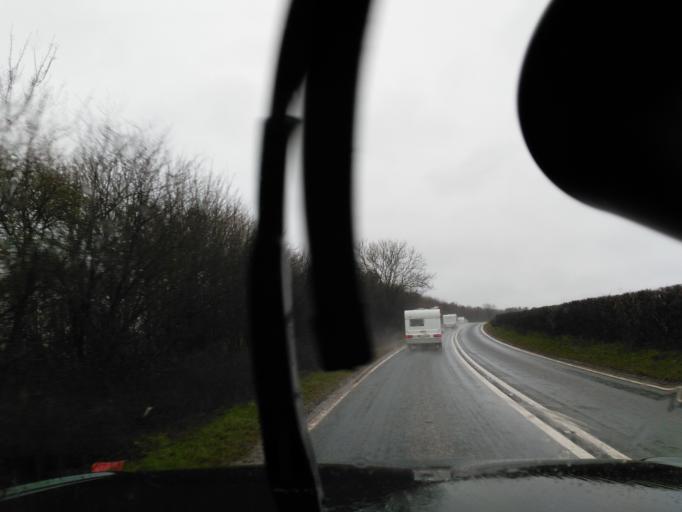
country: GB
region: England
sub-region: Somerset
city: Frome
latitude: 51.2011
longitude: -2.4036
